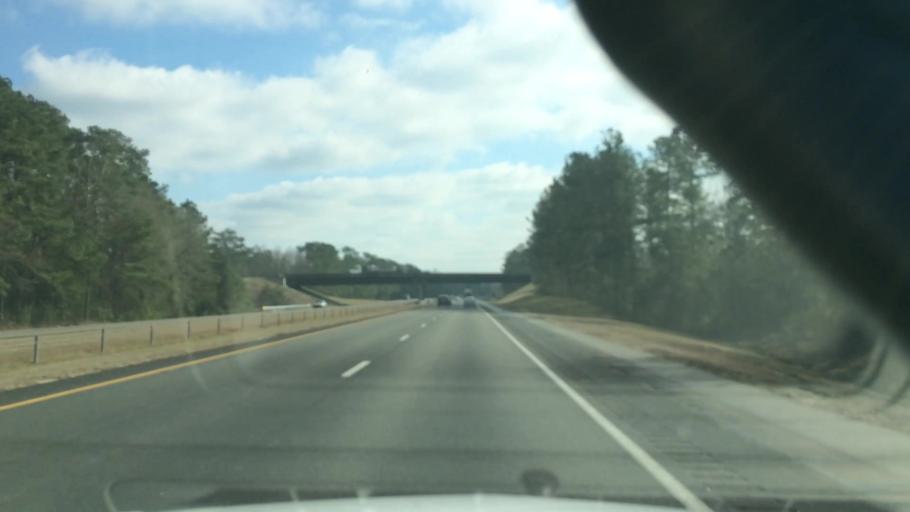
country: US
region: North Carolina
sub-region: Pender County
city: Burgaw
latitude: 34.6134
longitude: -77.9219
